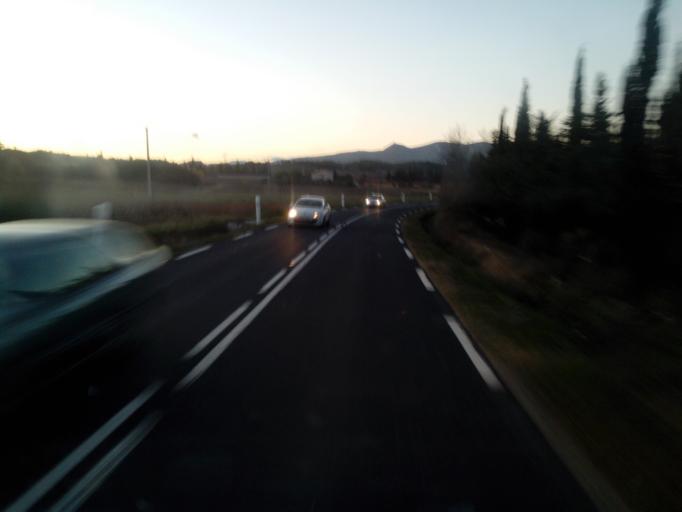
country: FR
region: Languedoc-Roussillon
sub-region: Departement des Pyrenees-Orientales
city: Peyrestortes
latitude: 42.7698
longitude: 2.8349
